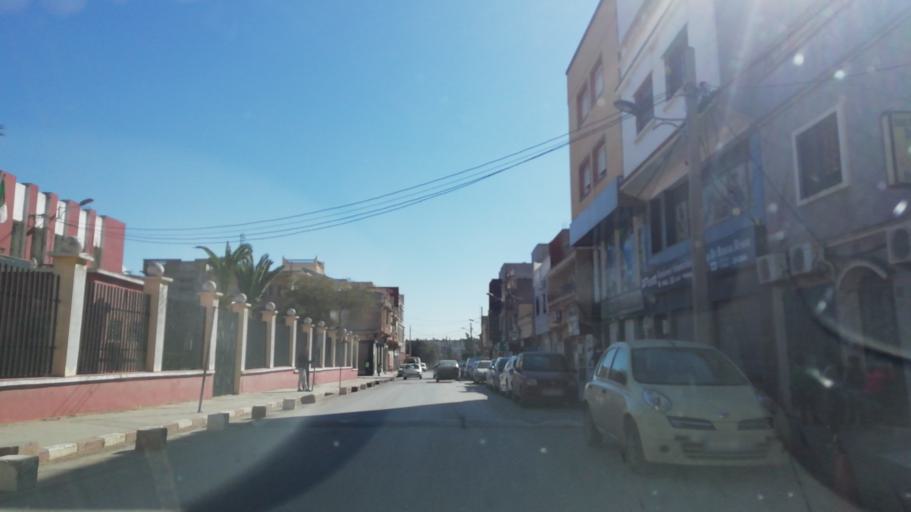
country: DZ
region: Oran
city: Oran
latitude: 35.6934
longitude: -0.6142
